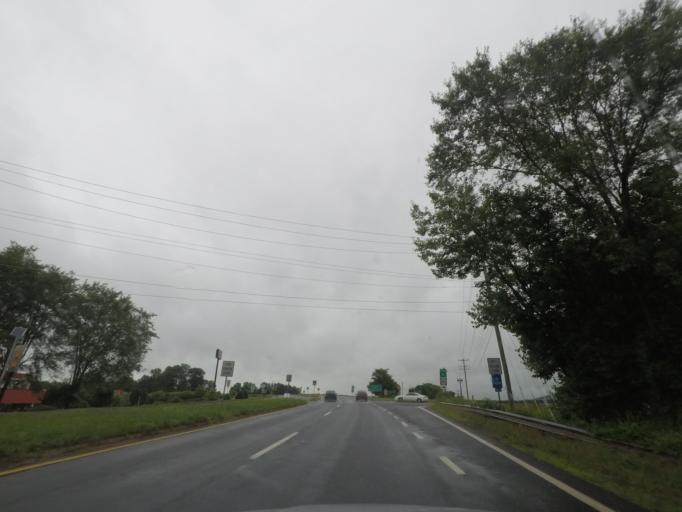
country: US
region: Virginia
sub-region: Culpeper County
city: Culpeper
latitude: 38.4444
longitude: -78.0112
